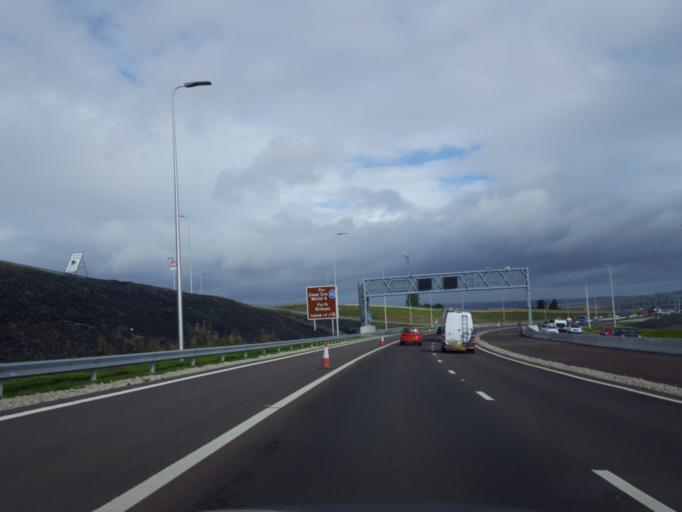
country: GB
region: Scotland
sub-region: Edinburgh
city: Queensferry
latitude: 55.9855
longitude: -3.4226
